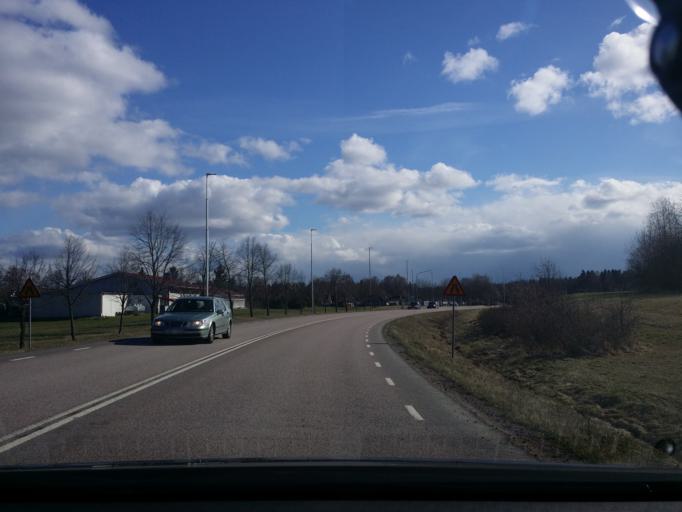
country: SE
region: Vaestmanland
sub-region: Sala Kommun
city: Sala
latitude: 59.9341
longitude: 16.5739
